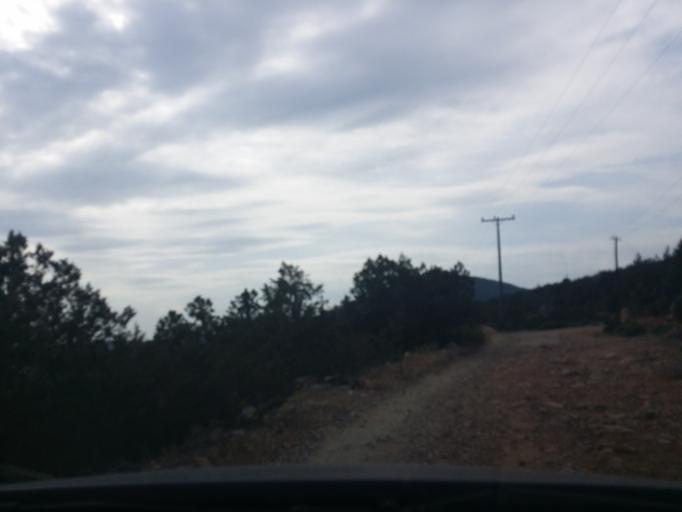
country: GR
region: Attica
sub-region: Nomos Piraios
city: Poros
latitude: 37.5432
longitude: 23.4821
